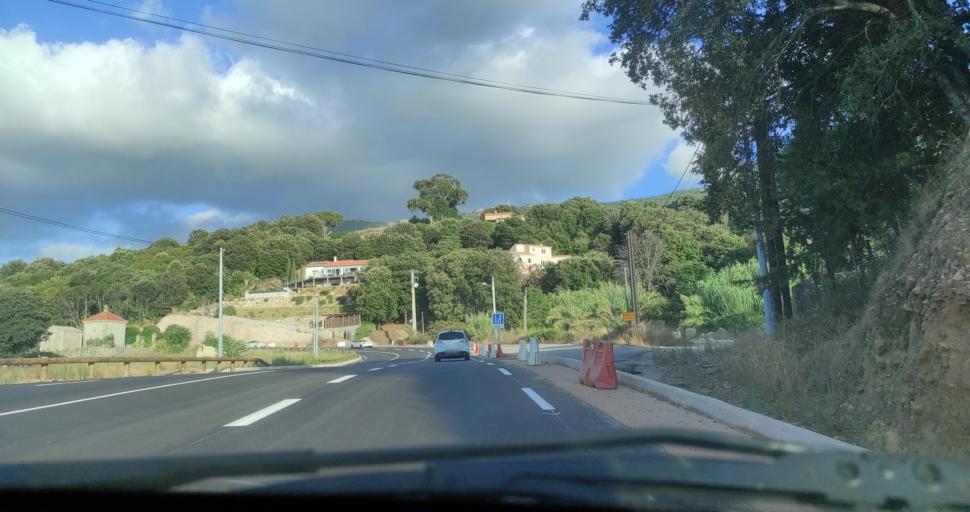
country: FR
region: Corsica
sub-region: Departement de la Corse-du-Sud
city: Appietto
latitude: 42.0344
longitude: 8.7606
